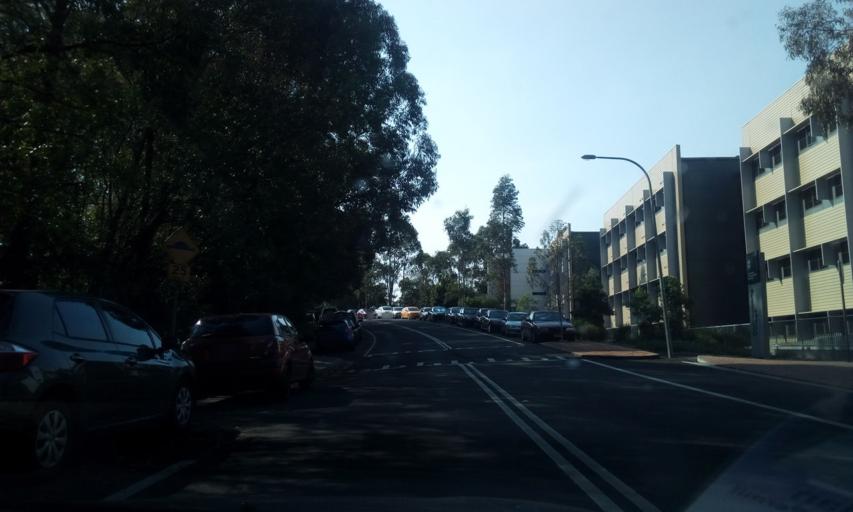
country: AU
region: New South Wales
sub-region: Wollongong
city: Mount Ousley
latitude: -34.4063
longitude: 150.8722
